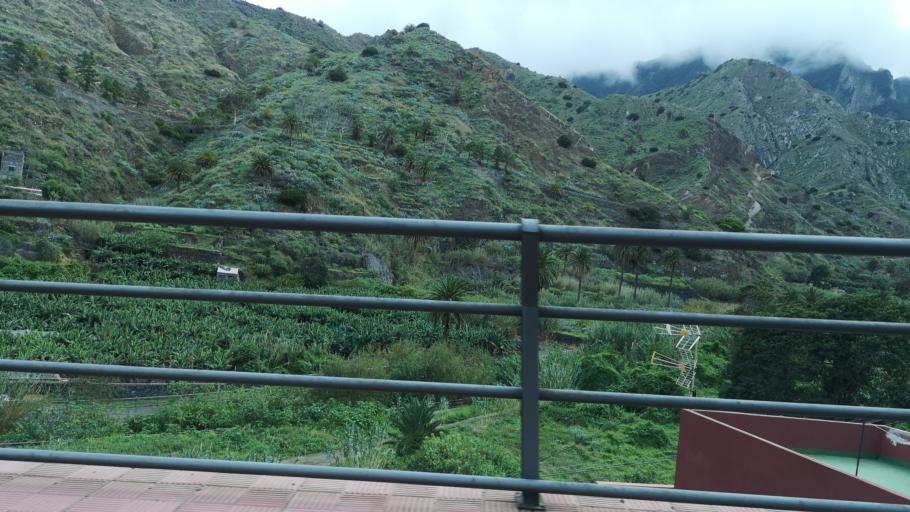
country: ES
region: Canary Islands
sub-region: Provincia de Santa Cruz de Tenerife
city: Hermigua
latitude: 28.1609
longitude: -17.1982
